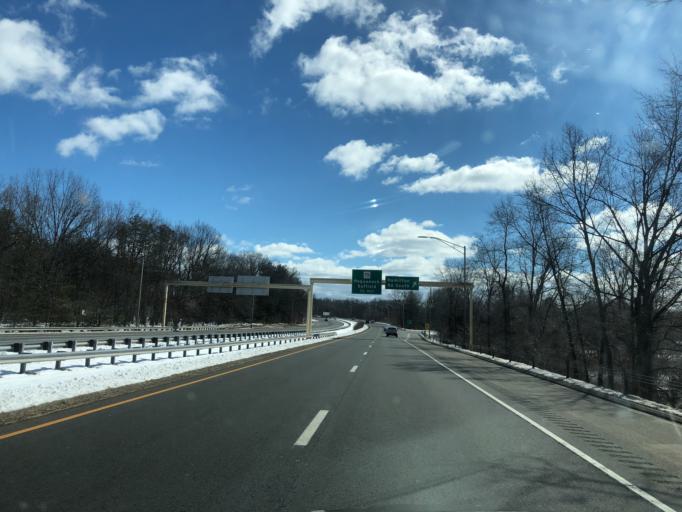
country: US
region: Connecticut
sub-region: Hartford County
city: Windsor Locks
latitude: 41.9192
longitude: -72.6913
